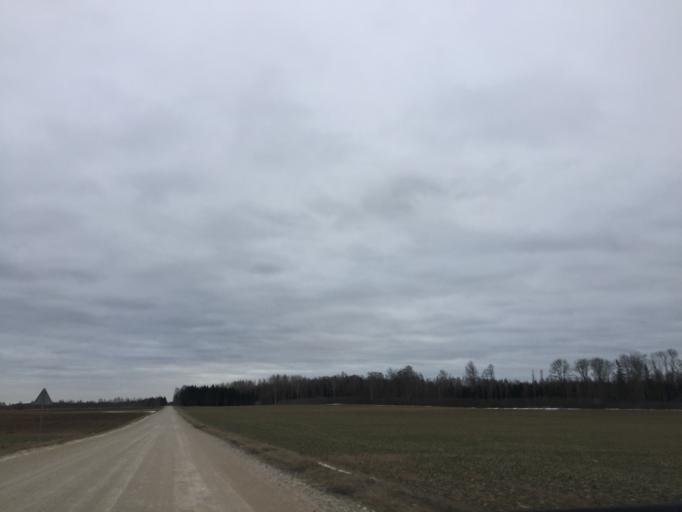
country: LT
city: Zagare
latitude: 56.3100
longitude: 23.2538
